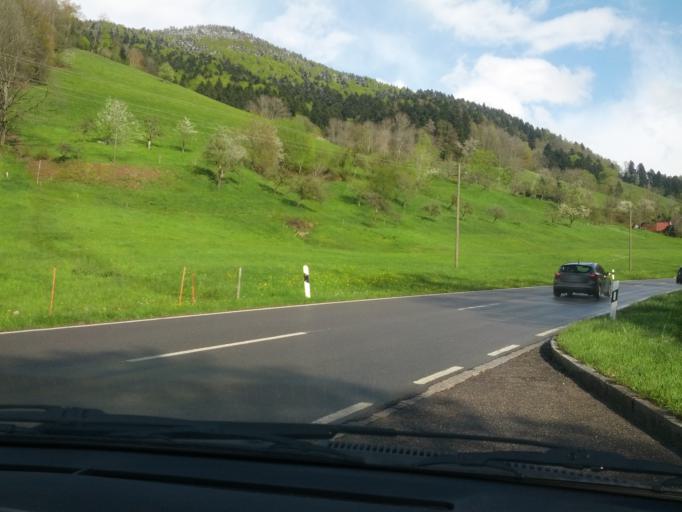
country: DE
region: Baden-Wuerttemberg
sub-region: Freiburg Region
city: Glottertal
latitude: 48.0390
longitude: 7.9857
